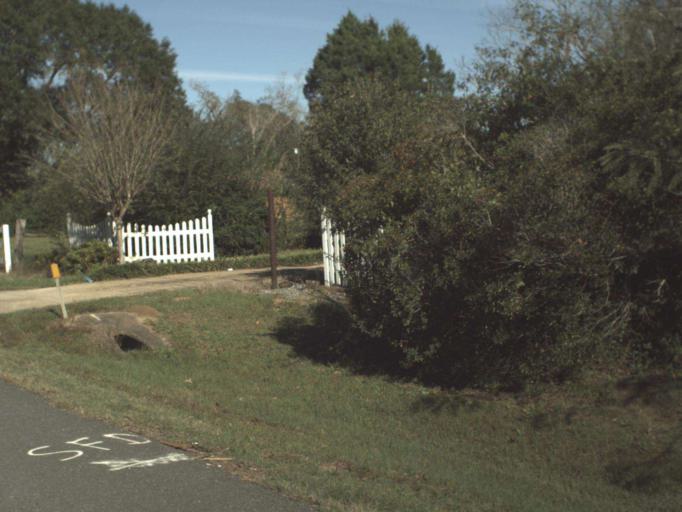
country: US
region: Florida
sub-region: Okaloosa County
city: Crestview
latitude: 30.7892
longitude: -86.6837
